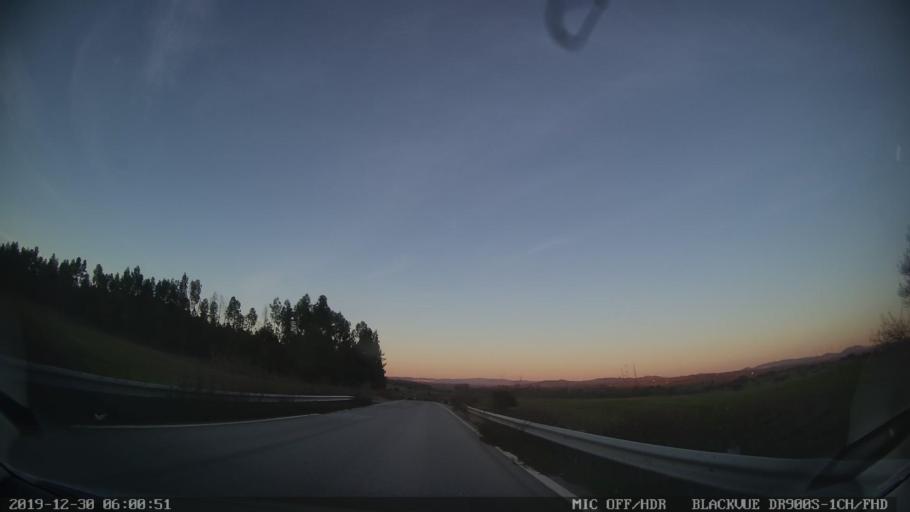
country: PT
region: Castelo Branco
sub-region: Idanha-A-Nova
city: Idanha-a-Nova
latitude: 40.0556
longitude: -7.2448
